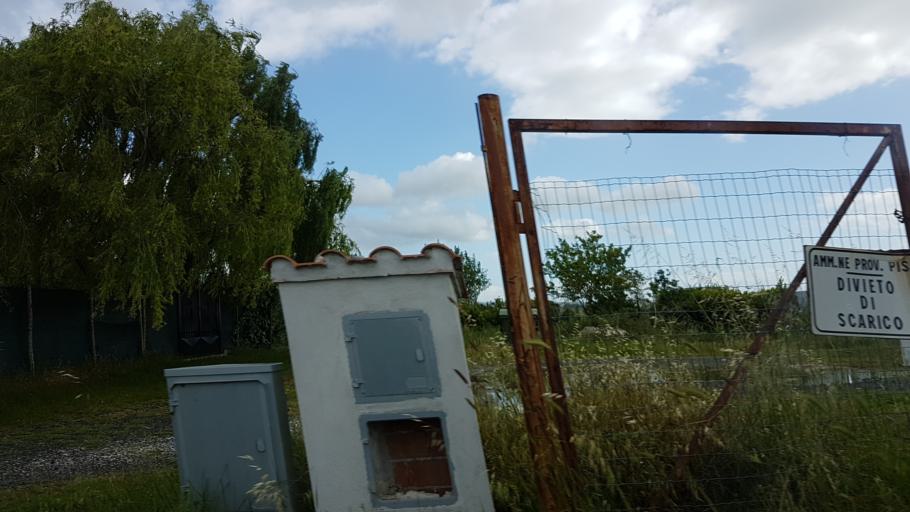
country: IT
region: Tuscany
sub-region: Province of Pisa
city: Santa Luce
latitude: 43.4678
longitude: 10.5554
